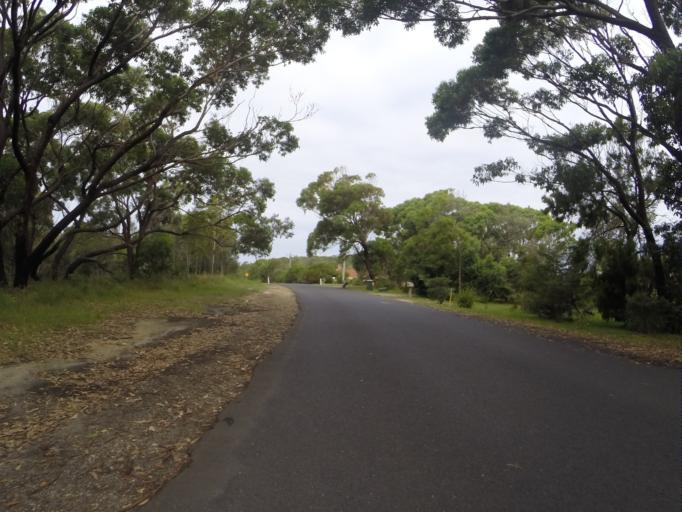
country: AU
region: New South Wales
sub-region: Eurobodalla
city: Broulee
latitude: -35.8299
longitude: 150.2205
